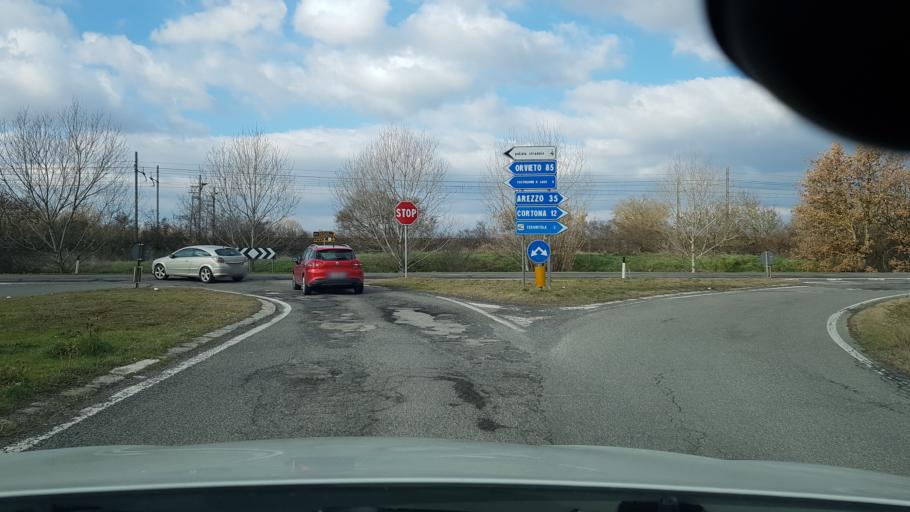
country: IT
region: Tuscany
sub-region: Province of Arezzo
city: Terontola
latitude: 43.1908
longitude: 12.0138
